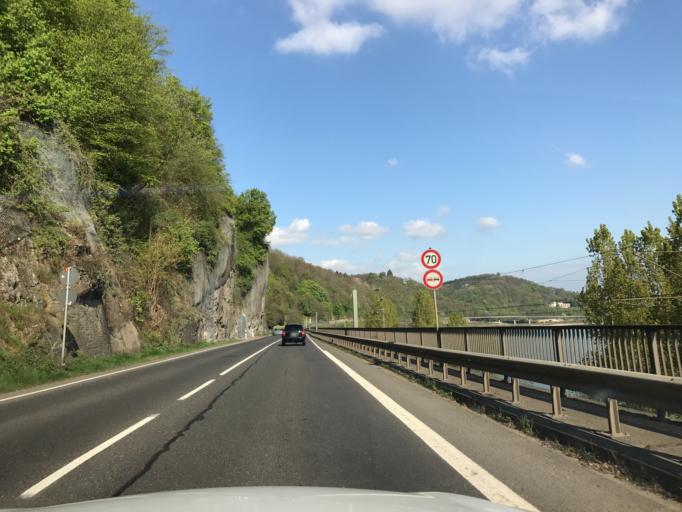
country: DE
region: Rheinland-Pfalz
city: Unkel
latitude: 50.5881
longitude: 7.2119
